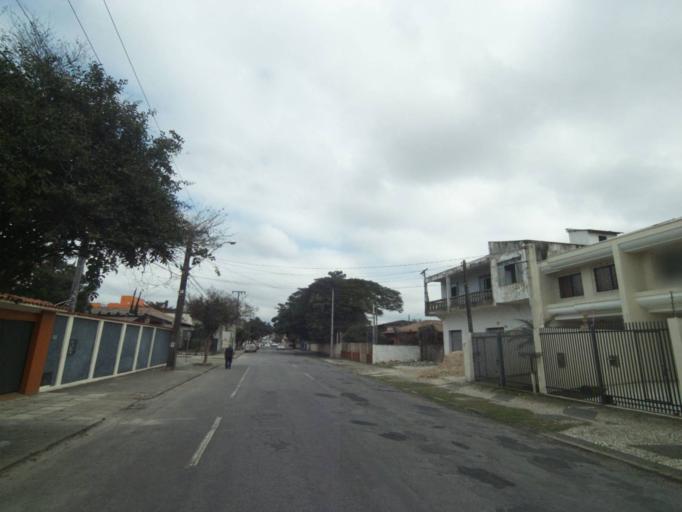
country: BR
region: Parana
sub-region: Paranagua
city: Paranagua
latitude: -25.5228
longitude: -48.5137
